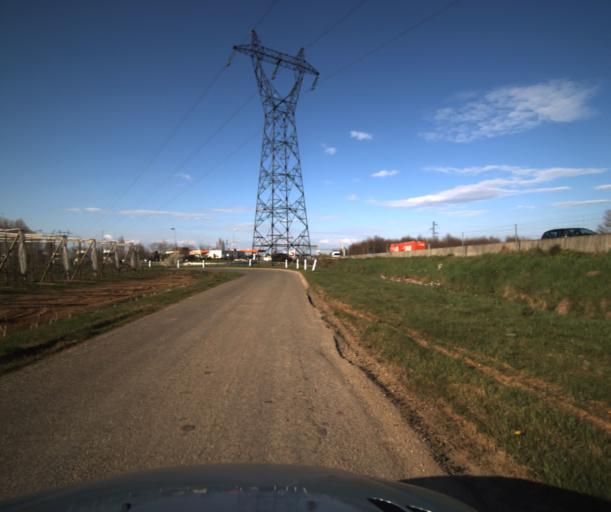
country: FR
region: Midi-Pyrenees
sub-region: Departement du Tarn-et-Garonne
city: Bressols
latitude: 43.9563
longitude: 1.3268
